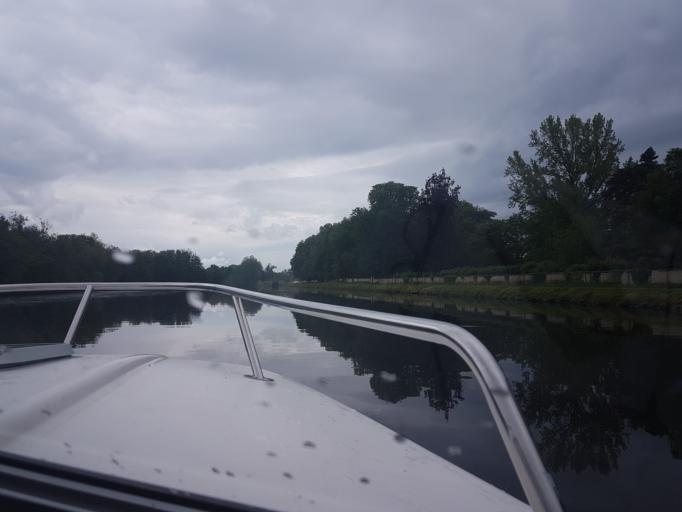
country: FR
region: Bourgogne
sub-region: Departement de l'Yonne
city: Saint-Bris-le-Vineux
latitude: 47.7007
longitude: 3.6380
